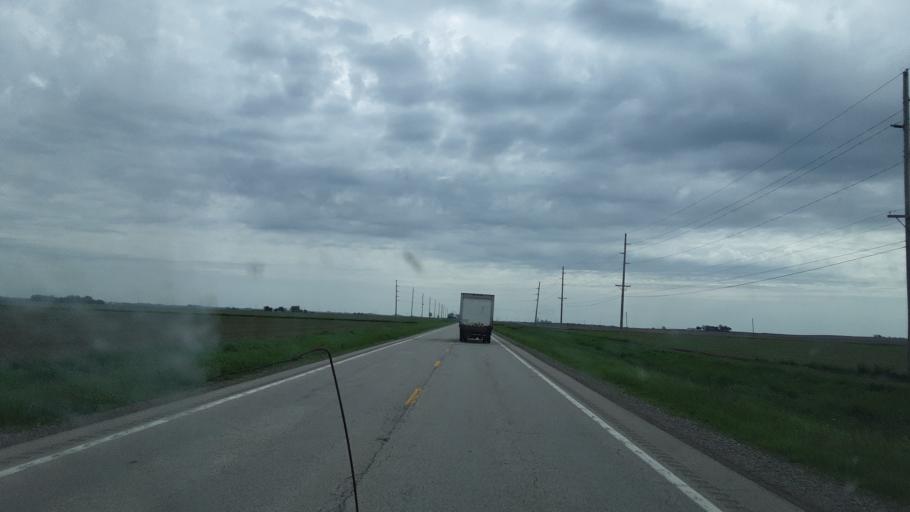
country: US
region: Illinois
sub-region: Tazewell County
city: Delavan
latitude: 40.3062
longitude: -89.5685
